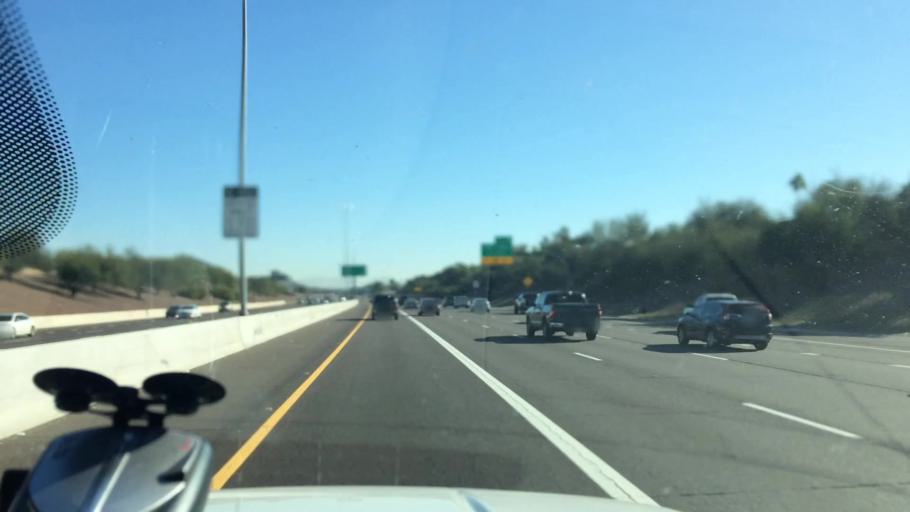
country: US
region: Arizona
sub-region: Maricopa County
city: Peoria
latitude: 33.6667
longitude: -112.2138
